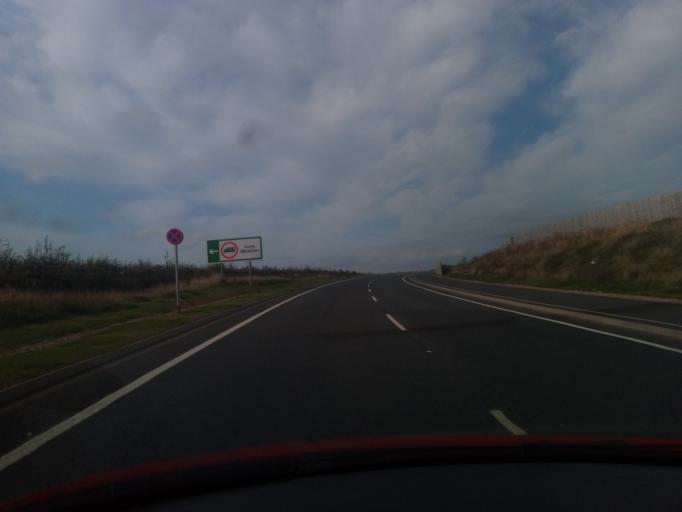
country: GB
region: England
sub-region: Leicestershire
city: Kegworth
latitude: 52.8299
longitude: -1.2885
